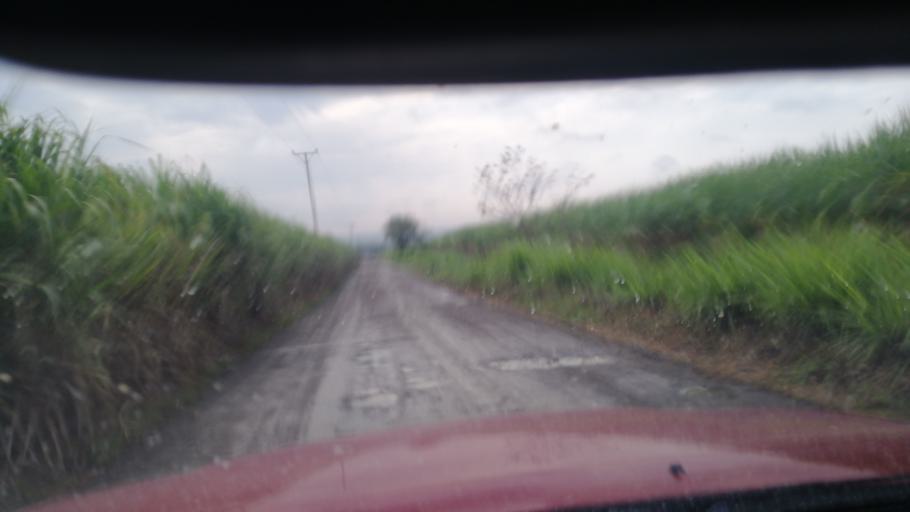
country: CO
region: Risaralda
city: La Virginia
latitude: 4.8760
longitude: -75.9259
